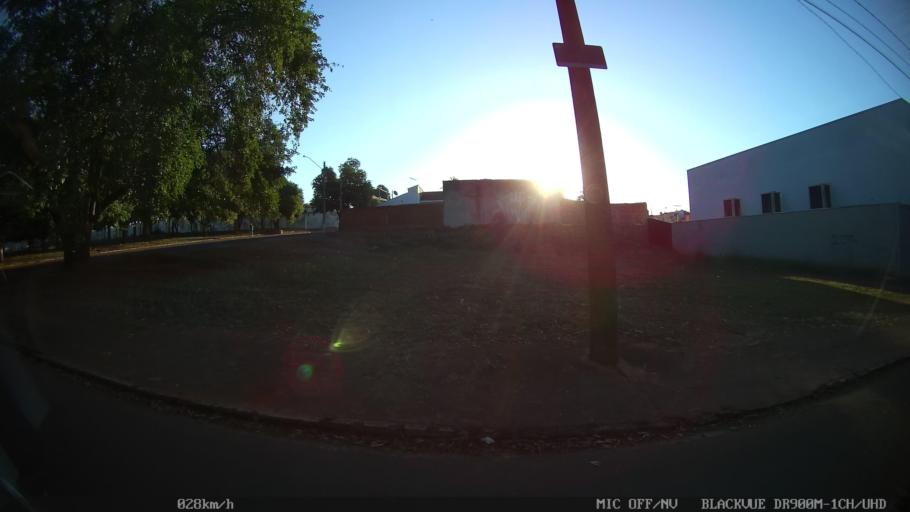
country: BR
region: Sao Paulo
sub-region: Sao Jose Do Rio Preto
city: Sao Jose do Rio Preto
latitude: -20.7755
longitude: -49.3556
